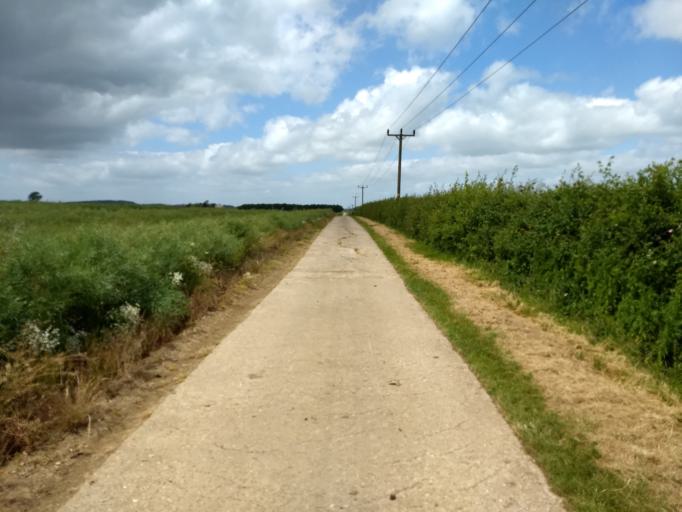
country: GB
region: England
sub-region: Milton Keynes
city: Calverton
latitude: 52.0146
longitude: -0.8349
